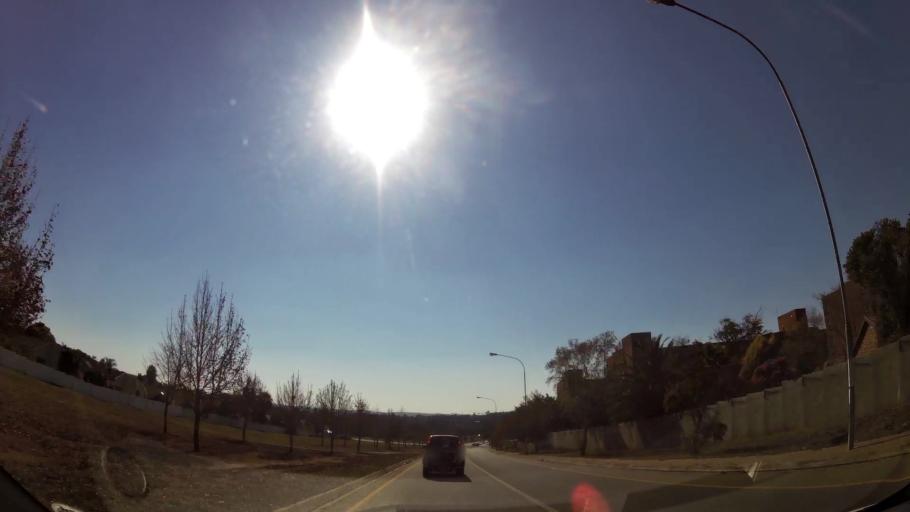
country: ZA
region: Gauteng
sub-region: City of Tshwane Metropolitan Municipality
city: Centurion
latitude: -25.8546
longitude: 28.1787
